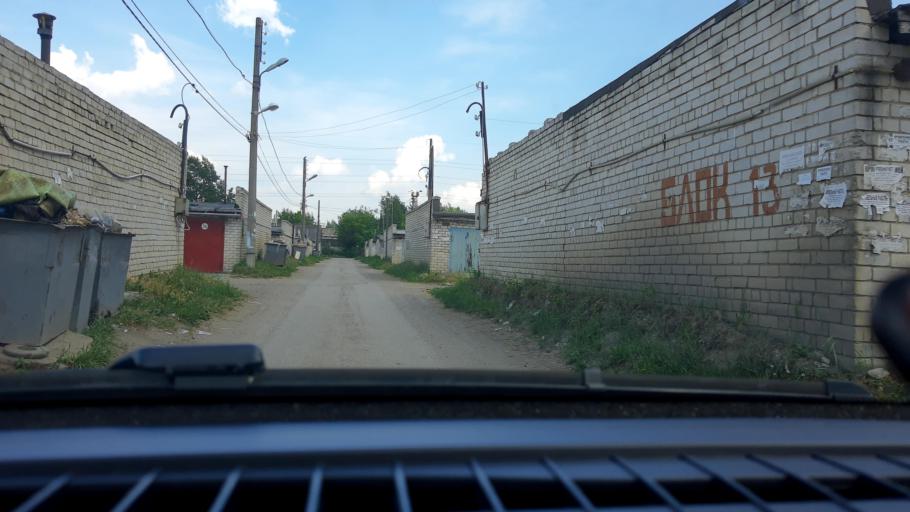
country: RU
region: Nizjnij Novgorod
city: Gorbatovka
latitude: 56.2697
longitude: 43.8458
